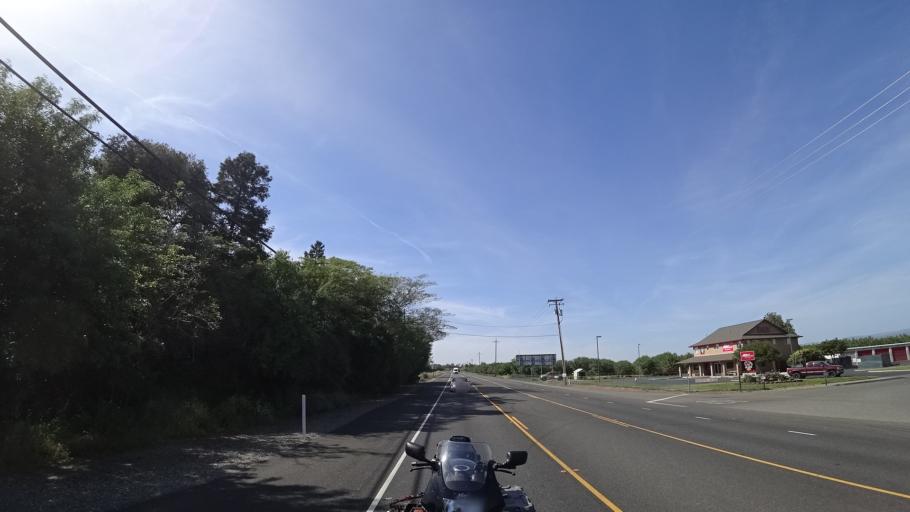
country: US
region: California
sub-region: Butte County
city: Chico
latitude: 39.7981
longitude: -121.9036
